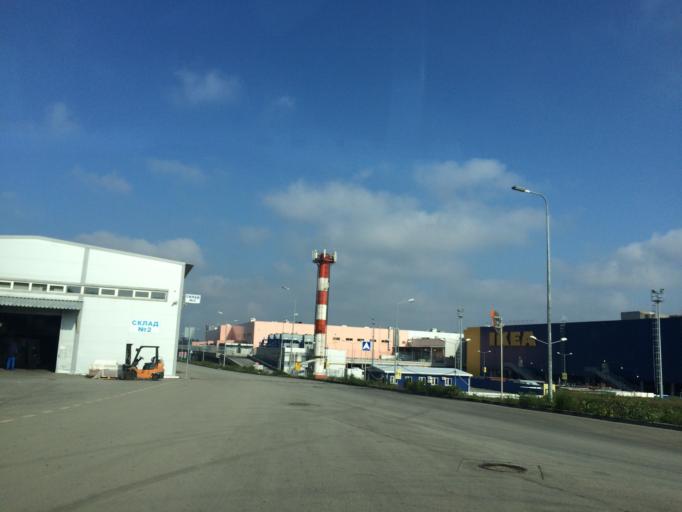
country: RU
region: Rostov
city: Aksay
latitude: 47.2870
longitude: 39.8440
